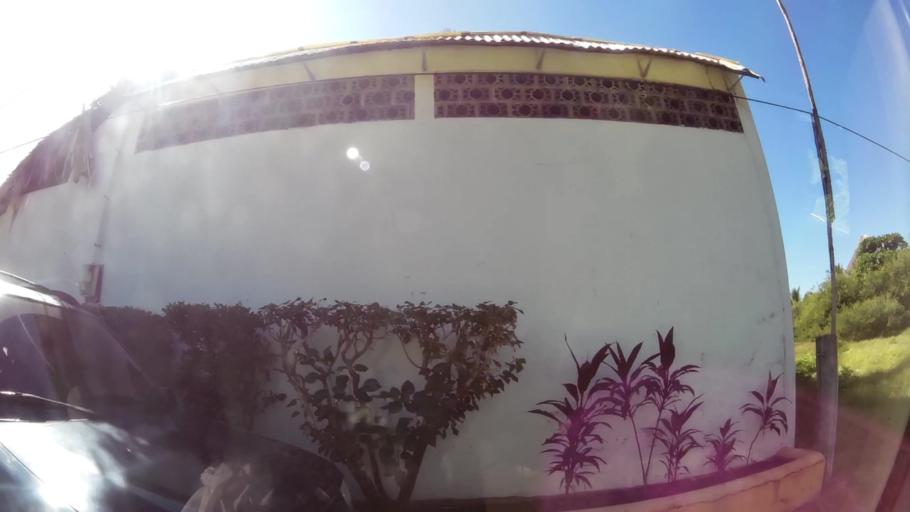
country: GT
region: Santa Rosa
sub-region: Municipio de Taxisco
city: Taxisco
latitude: 13.8812
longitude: -90.4550
